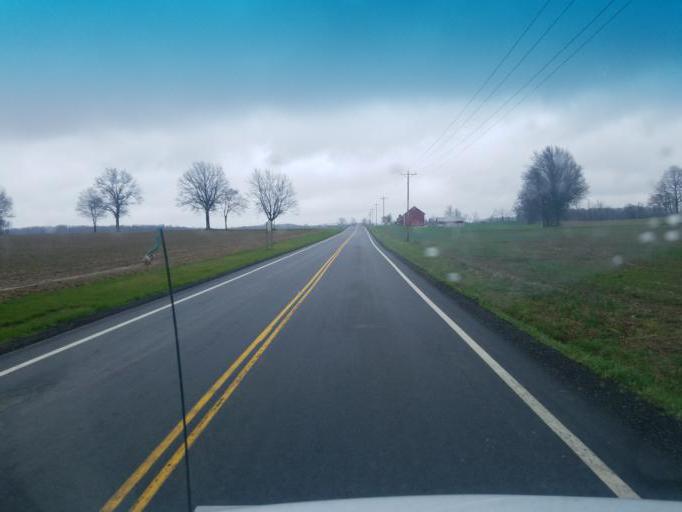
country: US
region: Ohio
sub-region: Huron County
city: Plymouth
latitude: 40.9602
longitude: -82.7545
